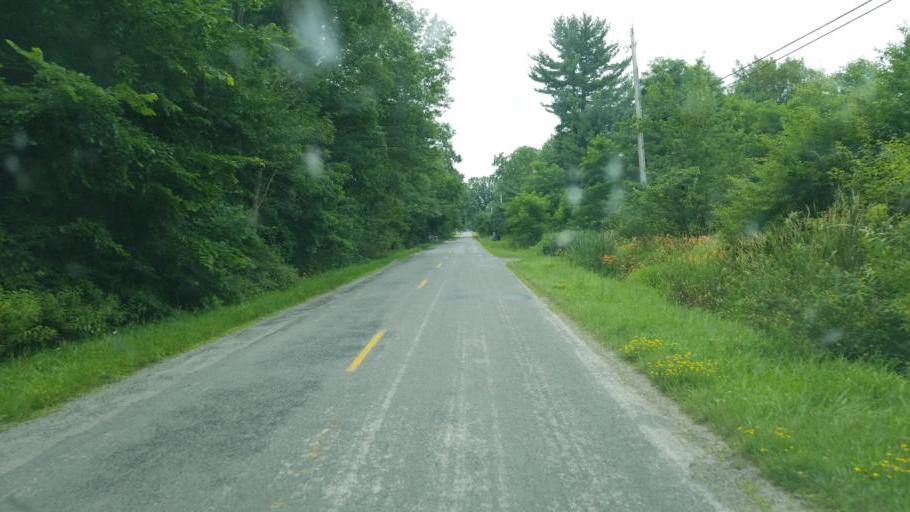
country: US
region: Ohio
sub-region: Trumbull County
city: Cortland
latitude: 41.4047
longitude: -80.7768
